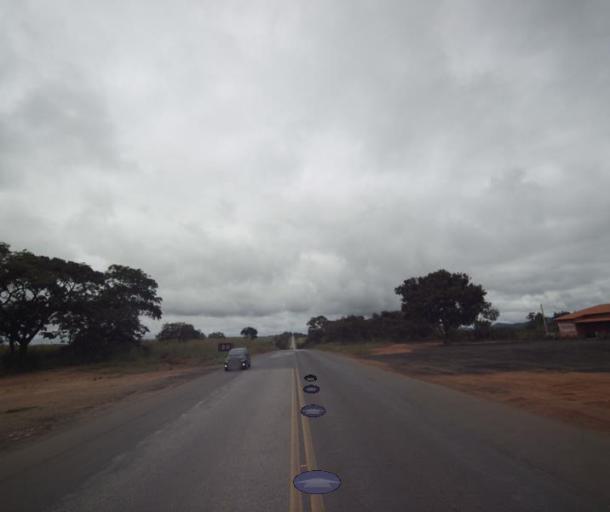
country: BR
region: Goias
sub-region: Uruacu
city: Uruacu
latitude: -14.6084
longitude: -49.1675
